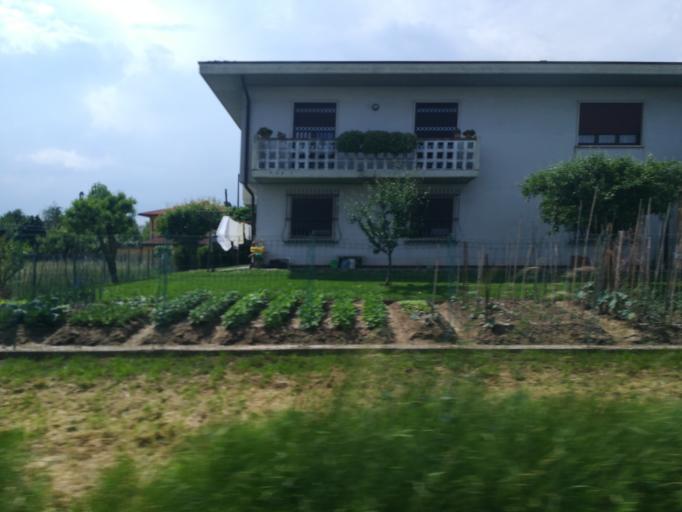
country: IT
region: Veneto
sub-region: Provincia di Vicenza
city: Monticello Conte Otto
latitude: 45.6077
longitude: 11.5703
